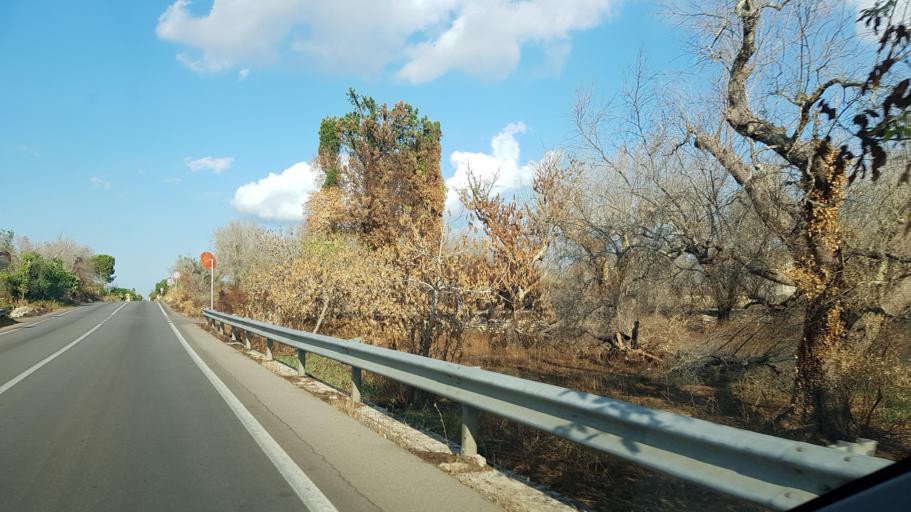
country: IT
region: Apulia
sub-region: Provincia di Lecce
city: Miggiano
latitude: 39.9642
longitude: 18.2943
